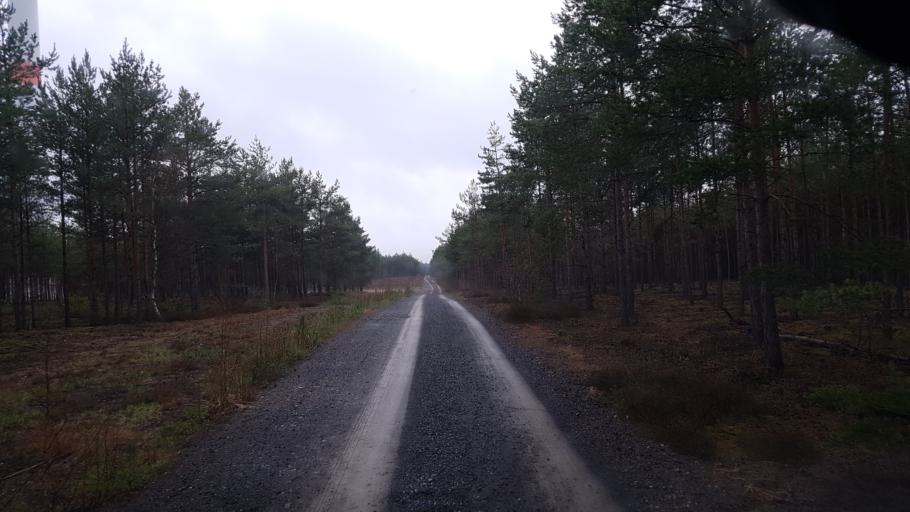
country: DE
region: Brandenburg
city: Grossraschen
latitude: 51.6135
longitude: 13.9623
